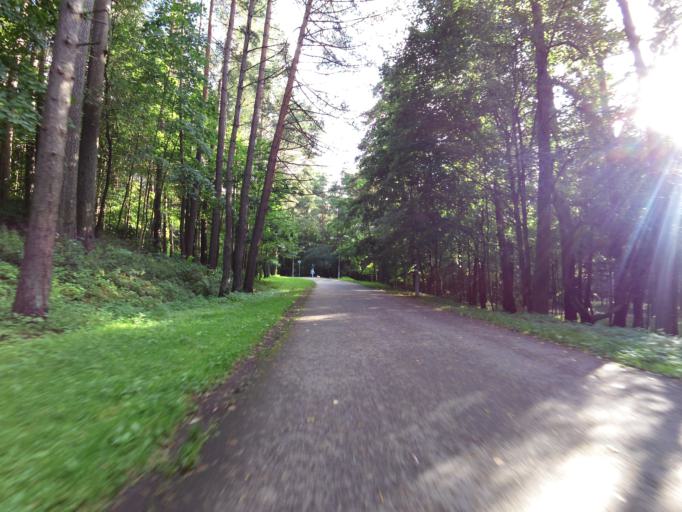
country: LT
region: Vilnius County
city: Vilkpede
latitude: 54.6784
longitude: 25.2406
